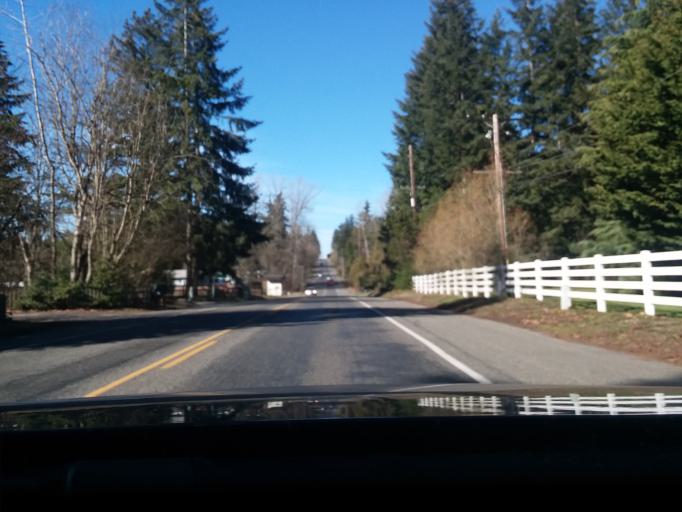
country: US
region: Washington
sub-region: Pierce County
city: Summit
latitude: 47.1620
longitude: -122.3387
